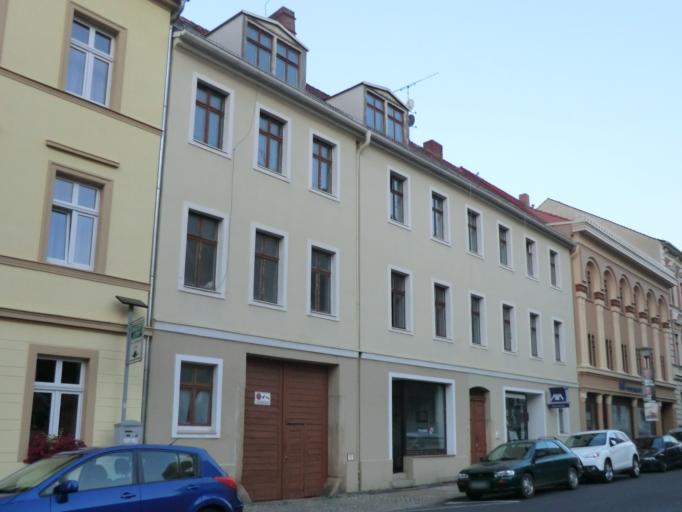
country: DE
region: Saxony
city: Goerlitz
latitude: 51.1508
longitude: 14.9877
